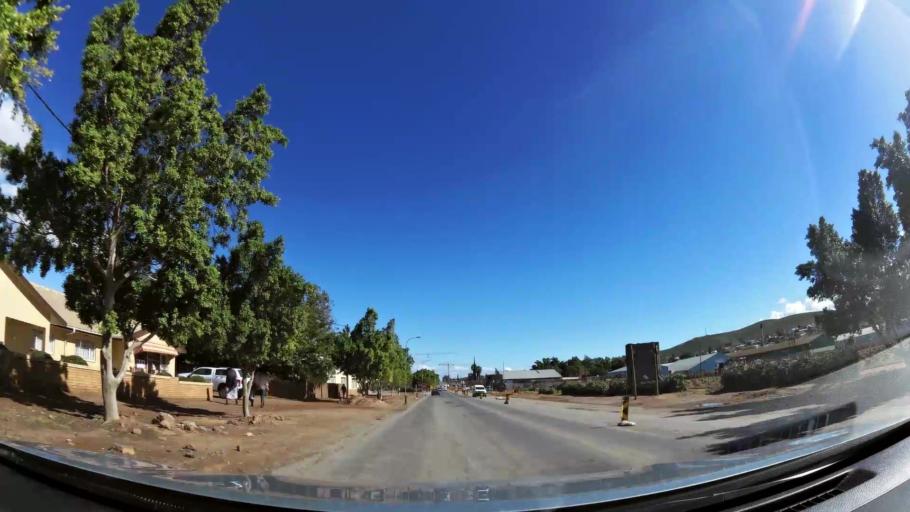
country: ZA
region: Western Cape
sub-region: Cape Winelands District Municipality
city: Ashton
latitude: -33.8327
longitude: 20.0674
